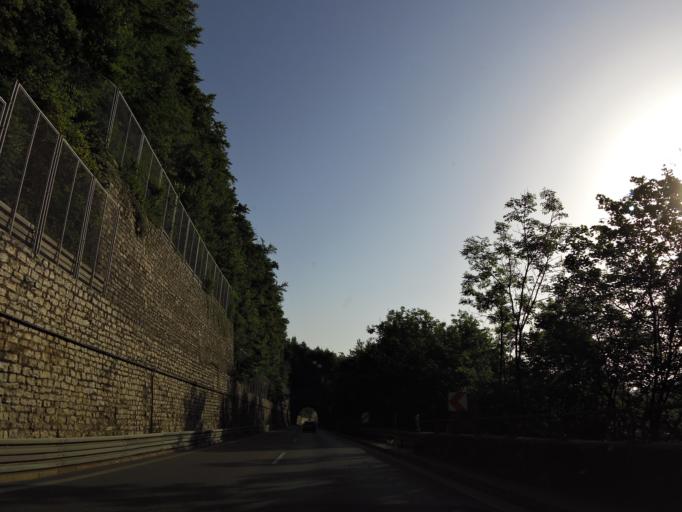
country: DE
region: Baden-Wuerttemberg
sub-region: Regierungsbezirk Stuttgart
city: Hohenstadt
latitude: 48.5568
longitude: 9.6613
